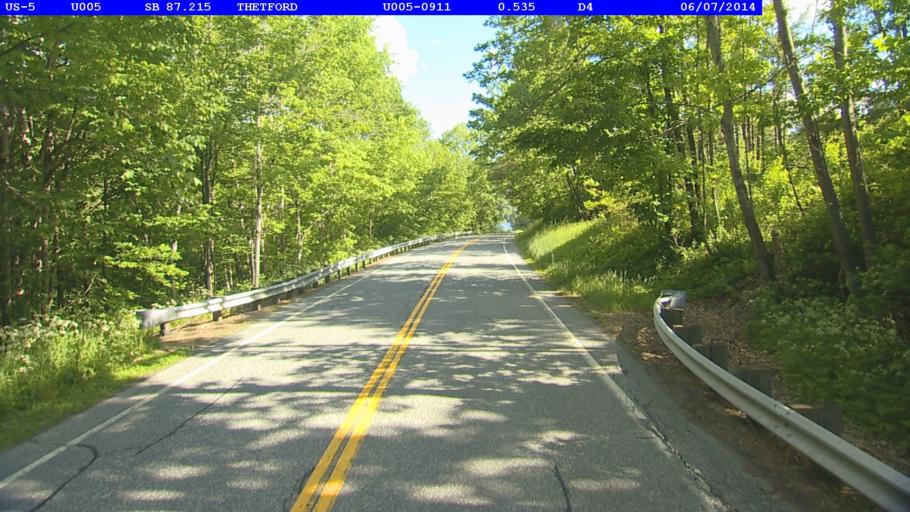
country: US
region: New Hampshire
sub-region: Grafton County
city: Lyme
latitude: 43.7794
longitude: -72.2059
